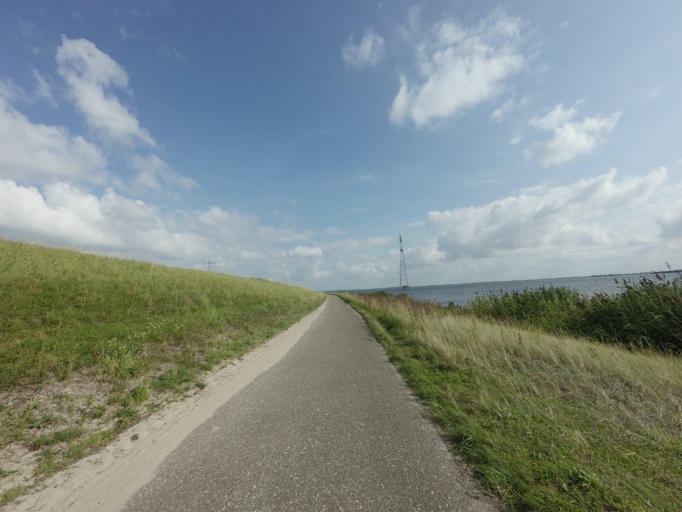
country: NL
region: Flevoland
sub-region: Gemeente Urk
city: Urk
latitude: 52.6148
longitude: 5.6555
